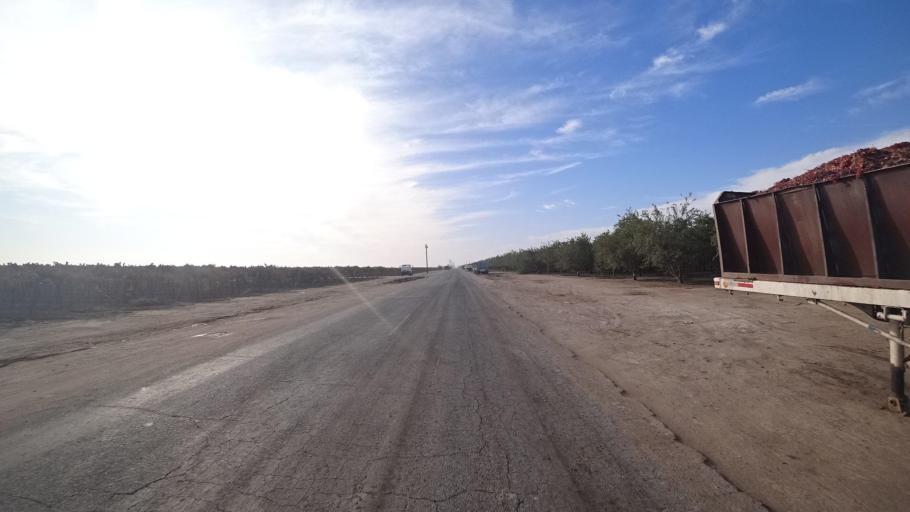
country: US
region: California
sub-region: Kern County
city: Delano
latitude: 35.7874
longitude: -119.2053
